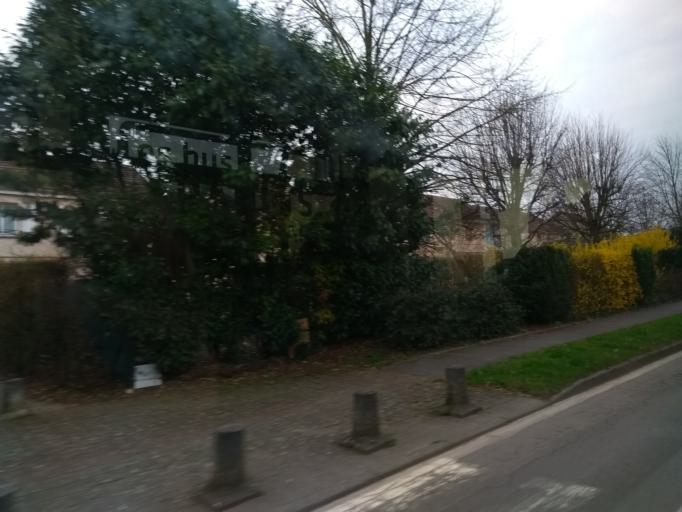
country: FR
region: Picardie
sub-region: Departement de l'Oise
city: Venette
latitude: 49.4213
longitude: 2.8055
